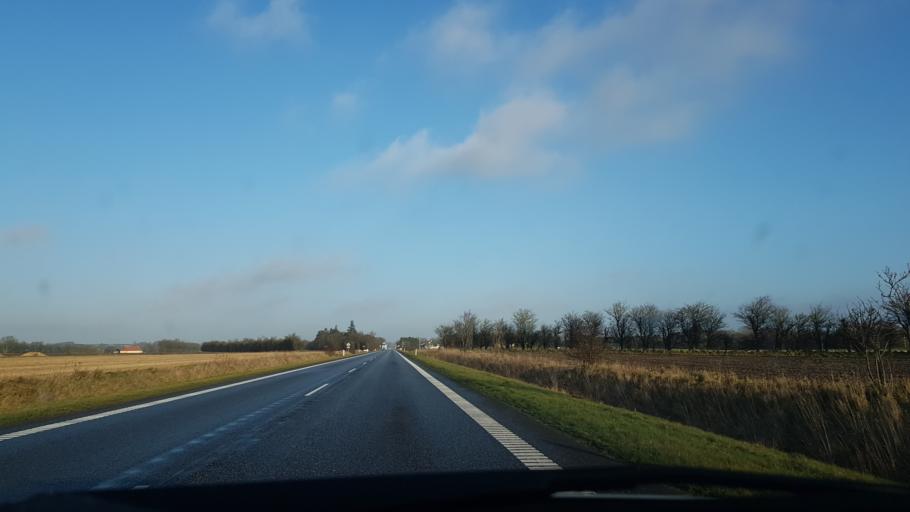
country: DK
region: South Denmark
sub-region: Tonder Kommune
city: Toftlund
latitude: 55.2277
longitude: 9.1156
